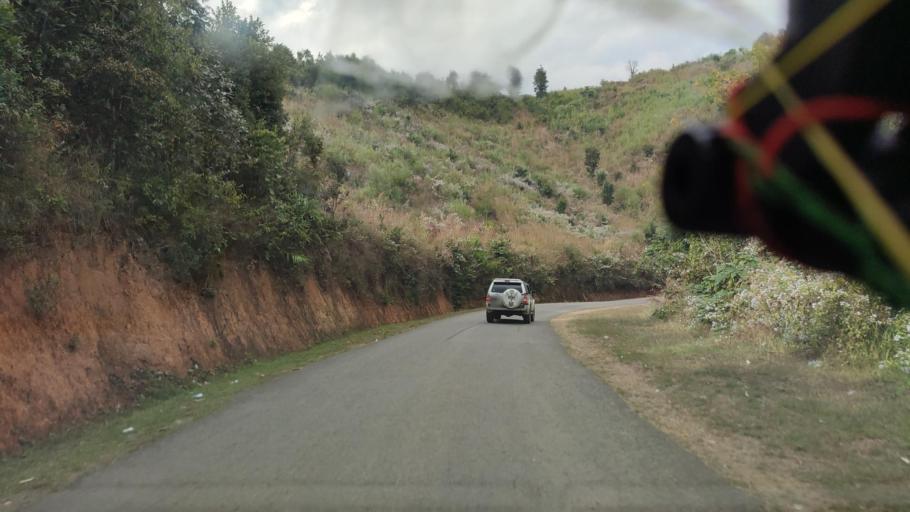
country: MM
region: Shan
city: Taunggyi
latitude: 21.2073
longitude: 97.6142
